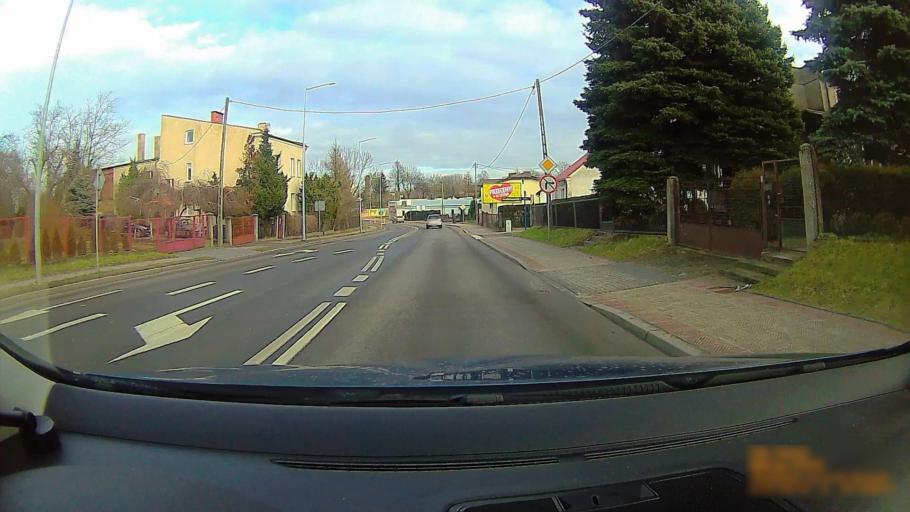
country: PL
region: Greater Poland Voivodeship
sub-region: Konin
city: Konin
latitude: 52.2018
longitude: 18.2466
